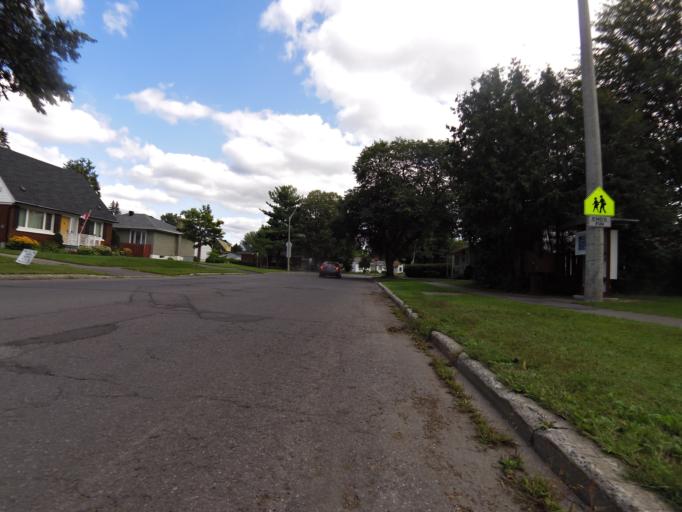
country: CA
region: Ontario
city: Ottawa
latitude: 45.3985
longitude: -75.6288
